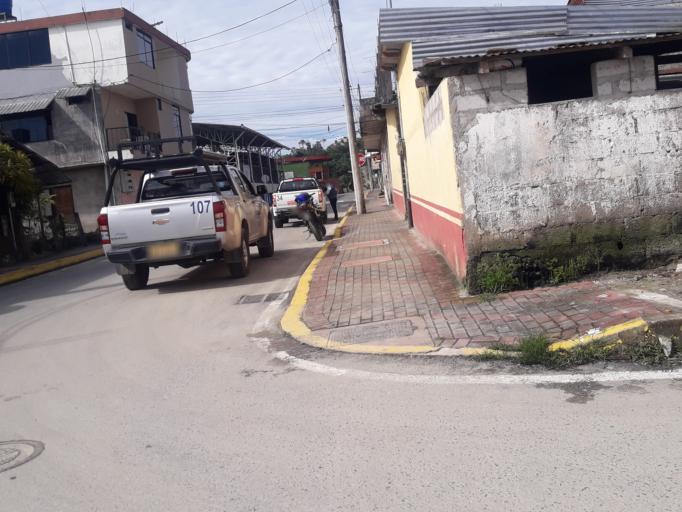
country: EC
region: Napo
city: Tena
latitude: -1.0034
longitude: -77.8136
